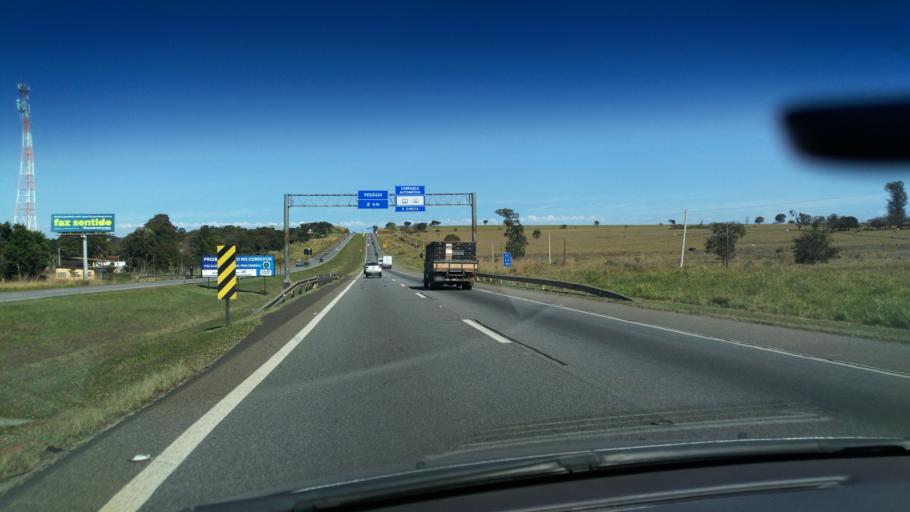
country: BR
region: Sao Paulo
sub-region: Jaguariuna
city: Jaguariuna
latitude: -22.7488
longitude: -47.0203
